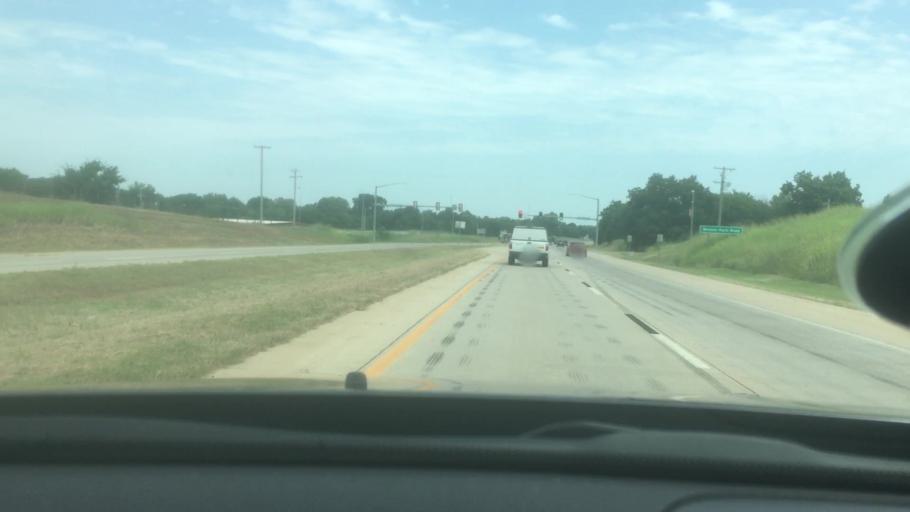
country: US
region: Oklahoma
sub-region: Pottawatomie County
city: Tecumseh
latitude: 35.2883
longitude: -96.9416
